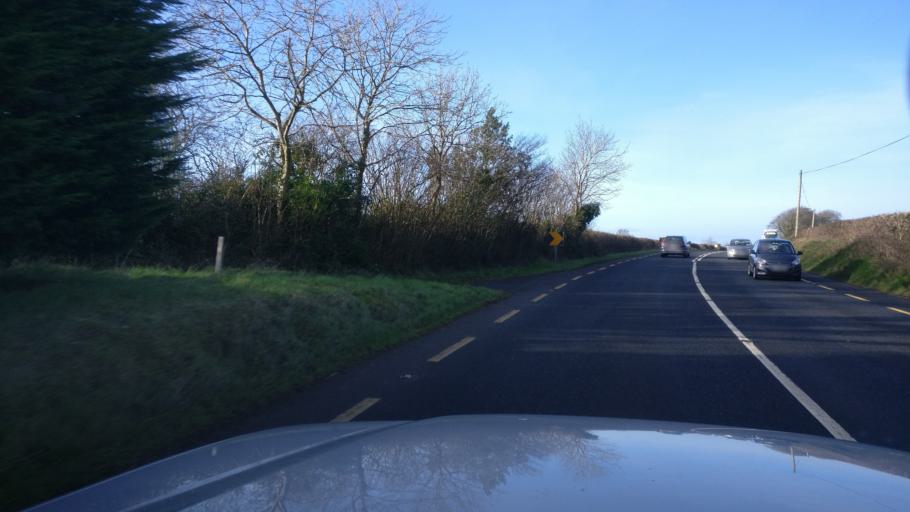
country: IE
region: Leinster
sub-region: Uibh Fhaili
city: Tullamore
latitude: 53.2002
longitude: -7.4309
